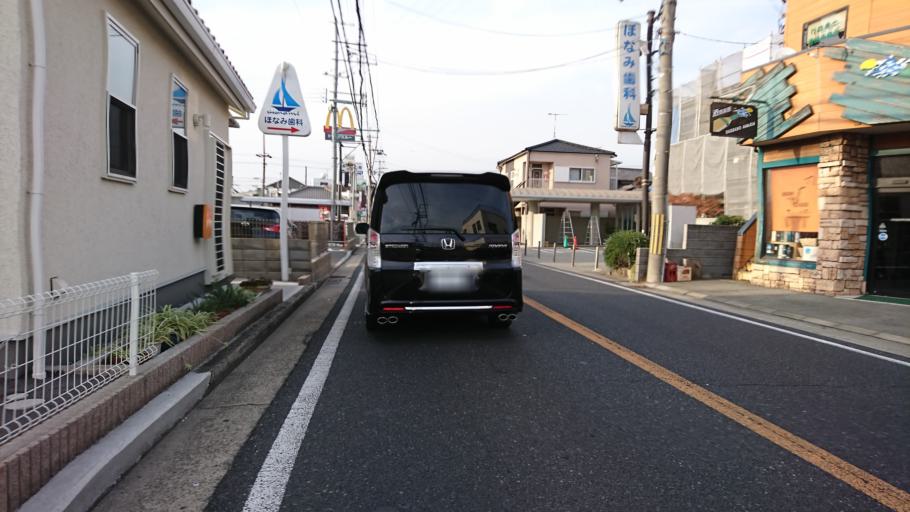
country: JP
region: Hyogo
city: Kakogawacho-honmachi
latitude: 34.7390
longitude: 134.8252
